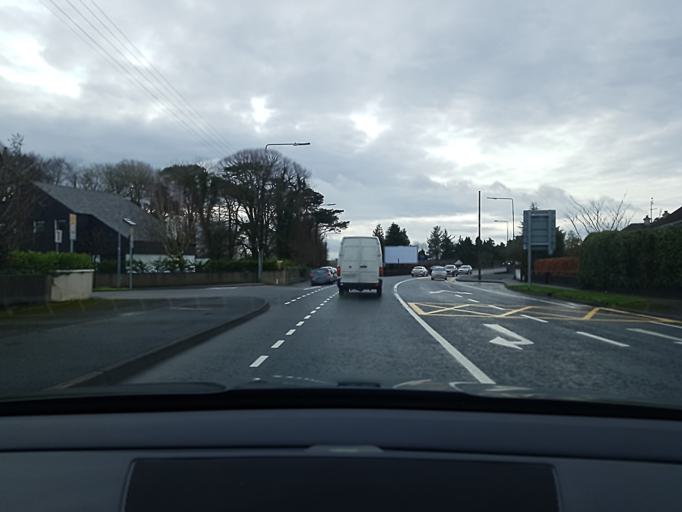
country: IE
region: Connaught
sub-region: Maigh Eo
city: Castlebar
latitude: 53.8490
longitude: -9.2887
